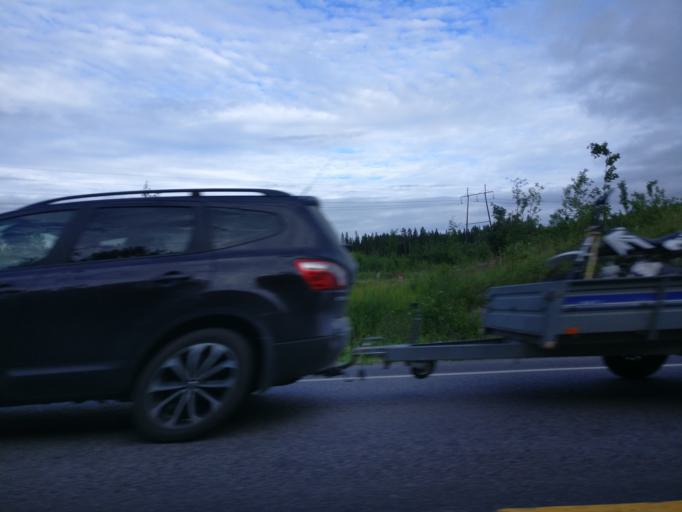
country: FI
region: Southern Savonia
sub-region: Savonlinna
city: Savonlinna
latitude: 61.8723
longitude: 28.9507
